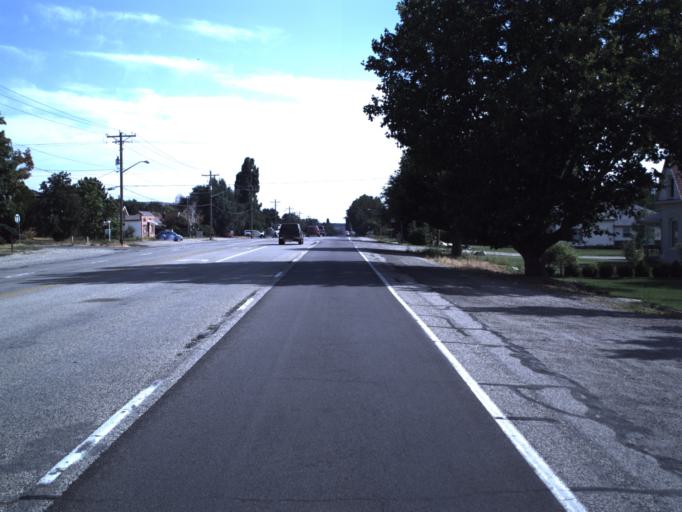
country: US
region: Utah
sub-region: Box Elder County
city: Willard
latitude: 41.4118
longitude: -112.0364
